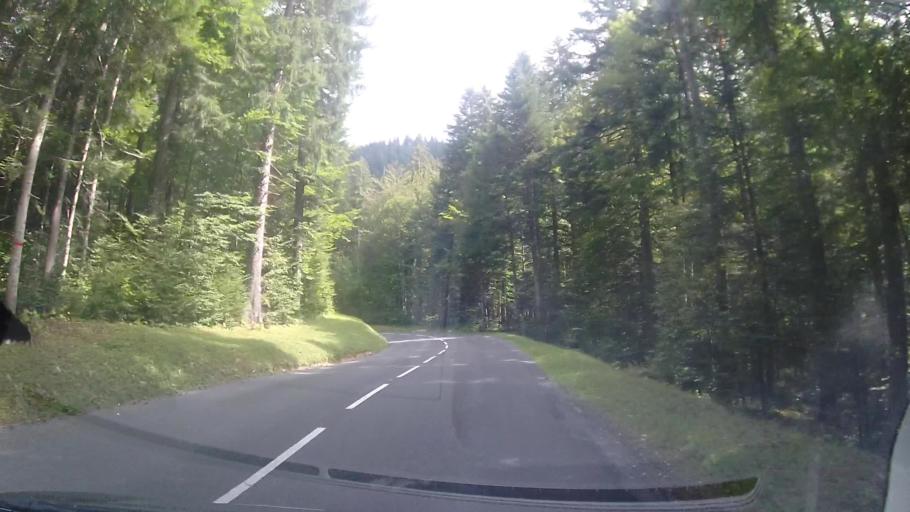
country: FR
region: Rhone-Alpes
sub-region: Departement de l'Ain
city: Gex
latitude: 46.3832
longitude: 6.0446
